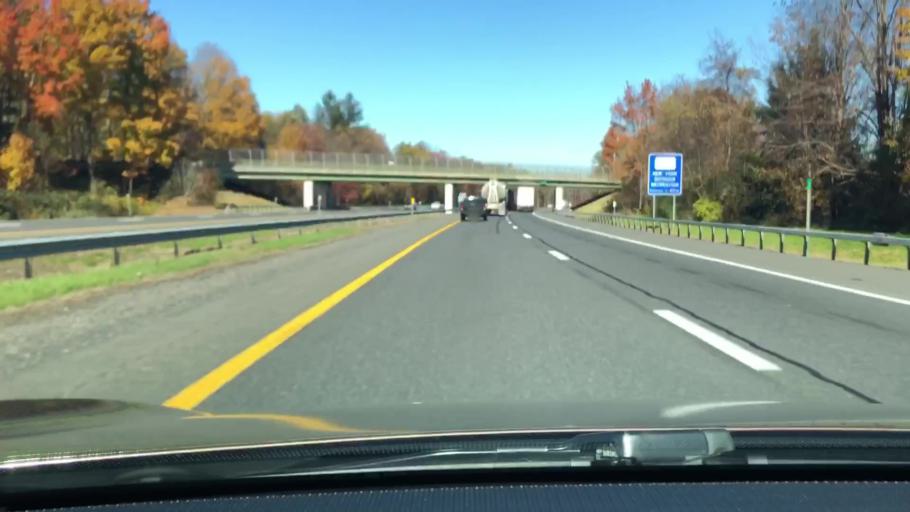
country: US
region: New York
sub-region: Ulster County
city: Clintondale
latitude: 41.6997
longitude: -74.0795
